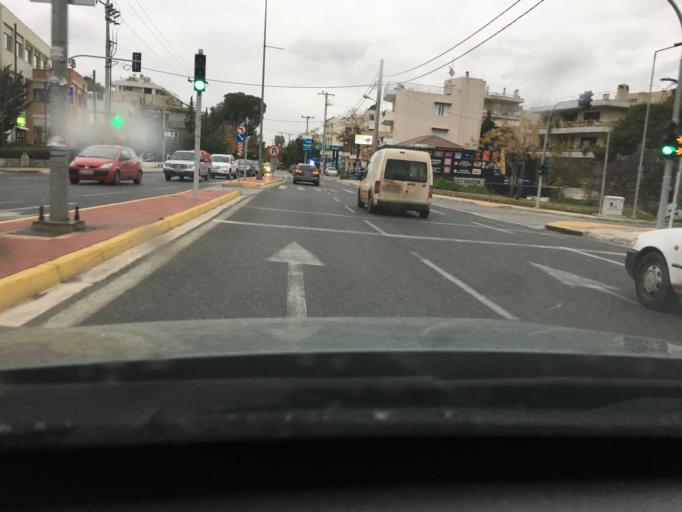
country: GR
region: Attica
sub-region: Nomarchia Athinas
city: Vrilissia
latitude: 38.0331
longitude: 23.8214
